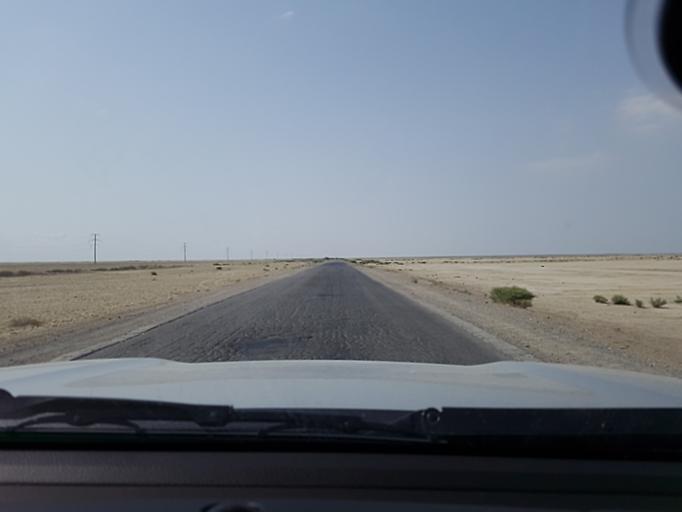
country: TM
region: Balkan
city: Gumdag
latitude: 38.9887
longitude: 54.5869
